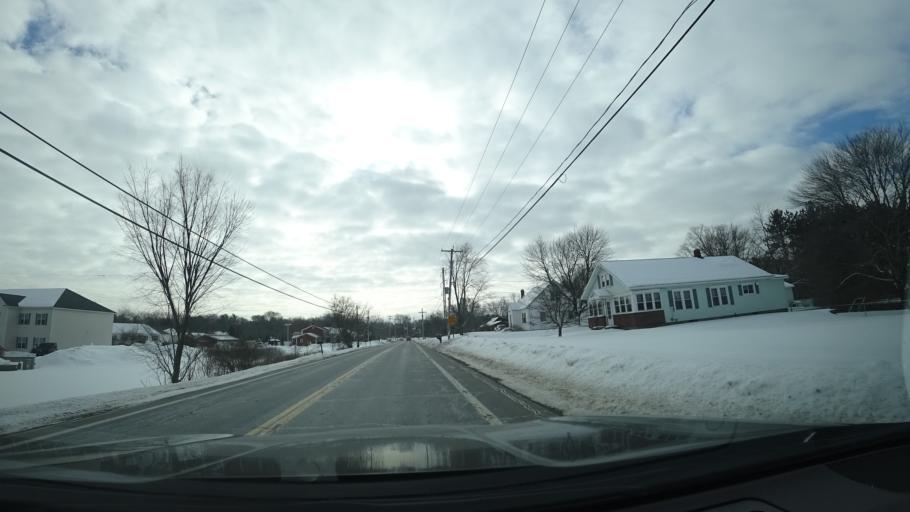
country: US
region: New York
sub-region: Saratoga County
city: South Glens Falls
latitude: 43.2865
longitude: -73.6235
